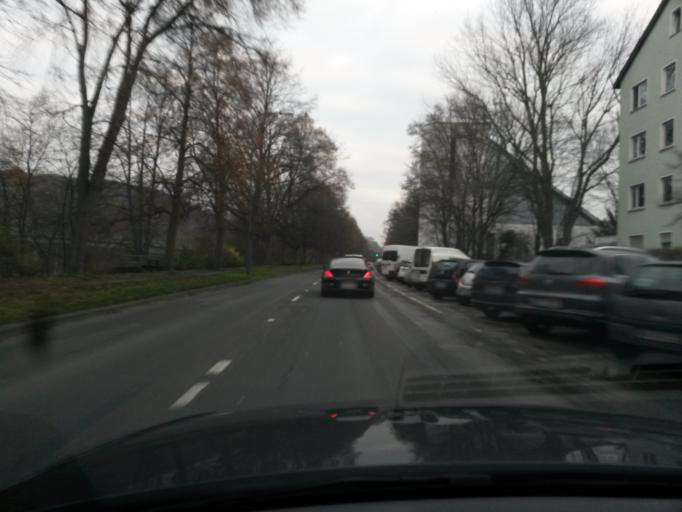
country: DE
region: Bavaria
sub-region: Regierungsbezirk Unterfranken
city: Wuerzburg
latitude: 49.7758
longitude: 9.9339
